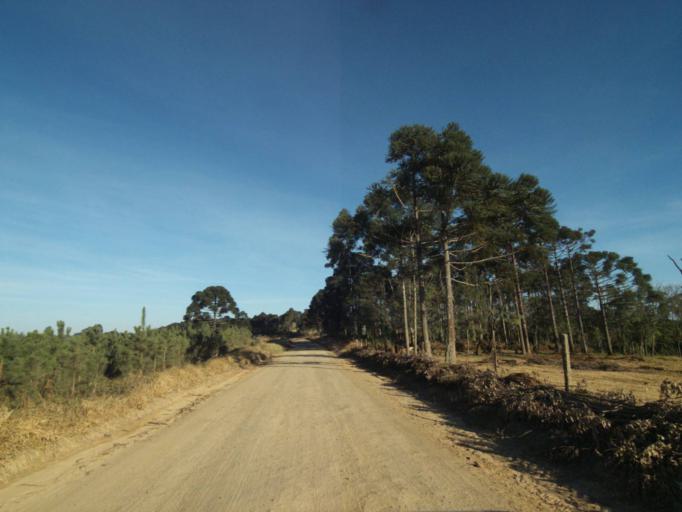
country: BR
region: Parana
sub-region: Telemaco Borba
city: Telemaco Borba
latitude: -24.5161
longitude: -50.6478
